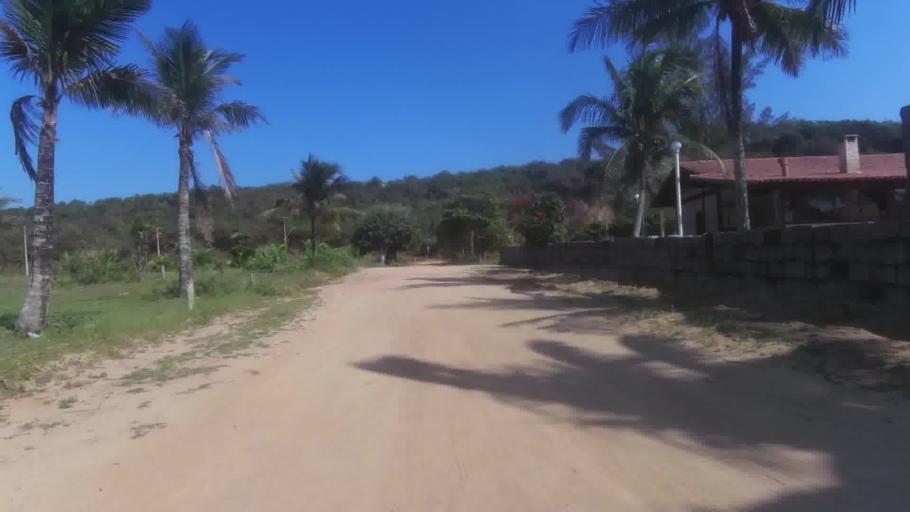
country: BR
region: Espirito Santo
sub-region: Marataizes
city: Marataizes
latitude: -21.0772
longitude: -40.8401
